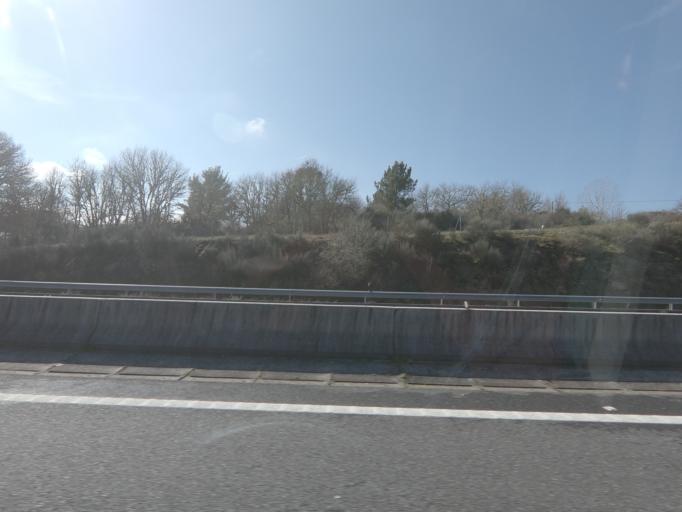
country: ES
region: Galicia
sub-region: Provincia de Ourense
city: Maside
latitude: 42.4119
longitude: -8.0126
